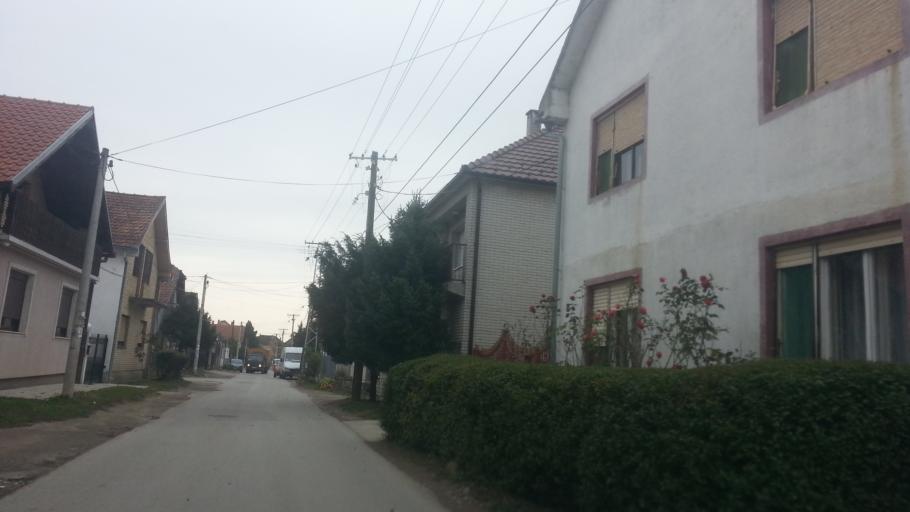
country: RS
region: Autonomna Pokrajina Vojvodina
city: Nova Pazova
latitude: 44.9522
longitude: 20.2132
